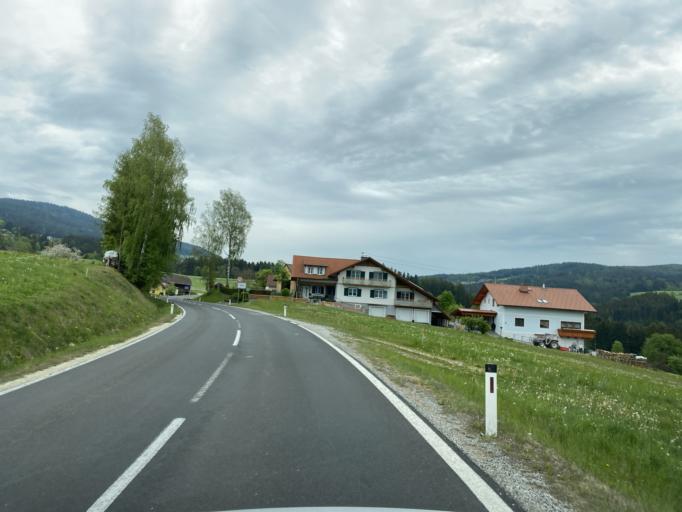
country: AT
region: Styria
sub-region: Politischer Bezirk Weiz
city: Gschaid bei Birkfeld
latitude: 47.3461
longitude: 15.7112
